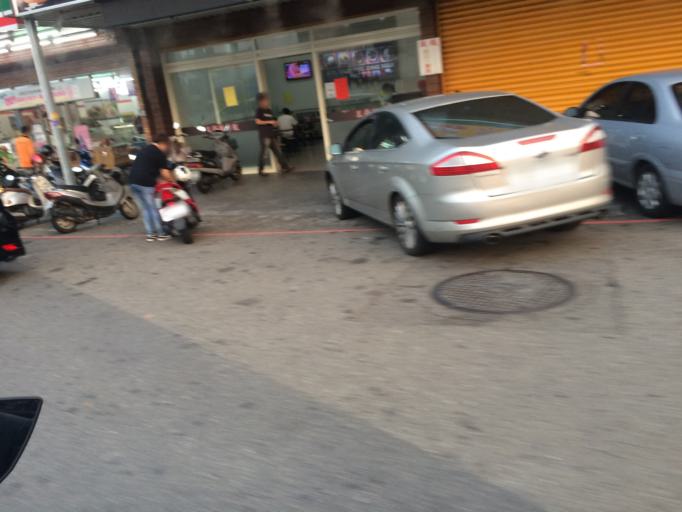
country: TW
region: Taiwan
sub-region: Hsinchu
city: Hsinchu
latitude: 24.6902
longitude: 120.9128
